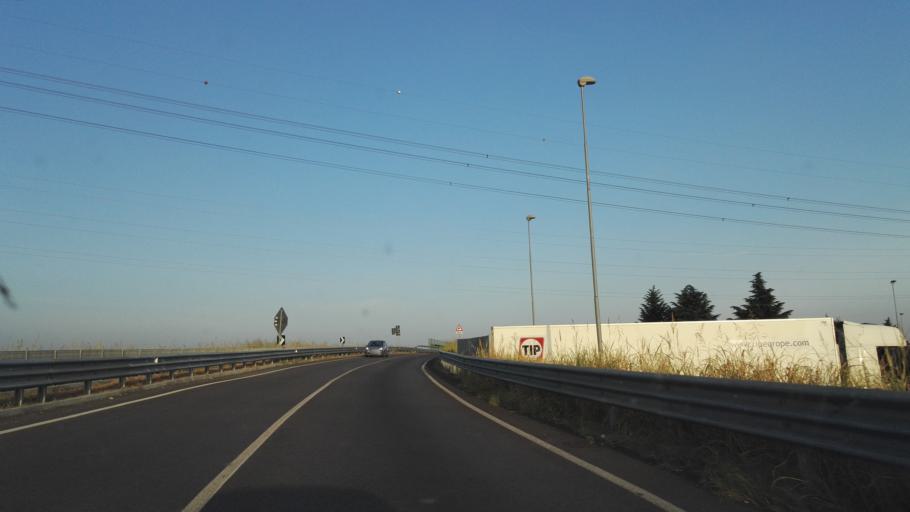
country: IT
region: Lombardy
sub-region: Citta metropolitana di Milano
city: Paullo
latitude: 45.4177
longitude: 9.4159
